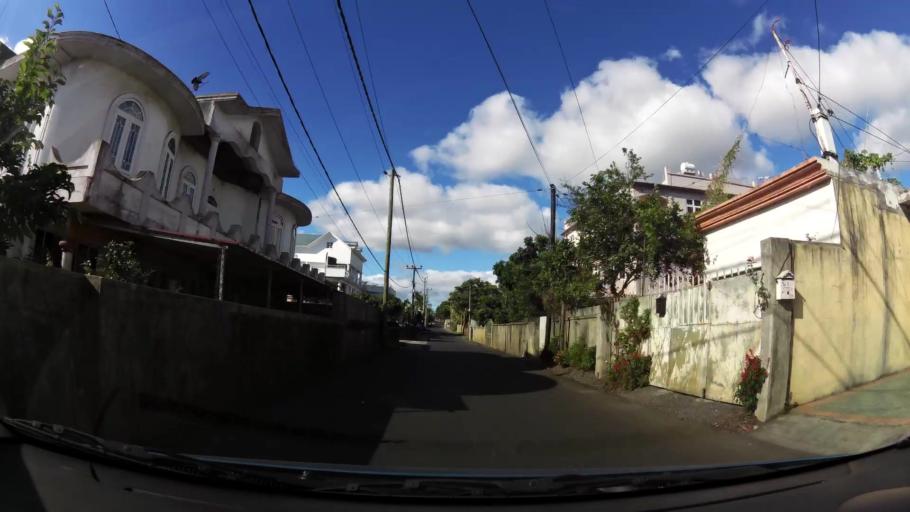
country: MU
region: Plaines Wilhems
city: Vacoas
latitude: -20.2852
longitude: 57.4856
